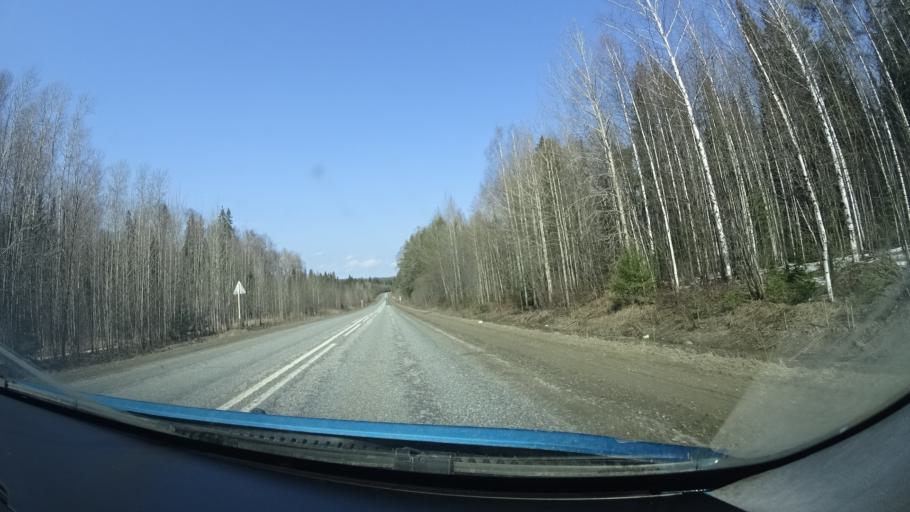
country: RU
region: Perm
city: Yugo-Kamskiy
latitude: 57.5200
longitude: 55.6853
